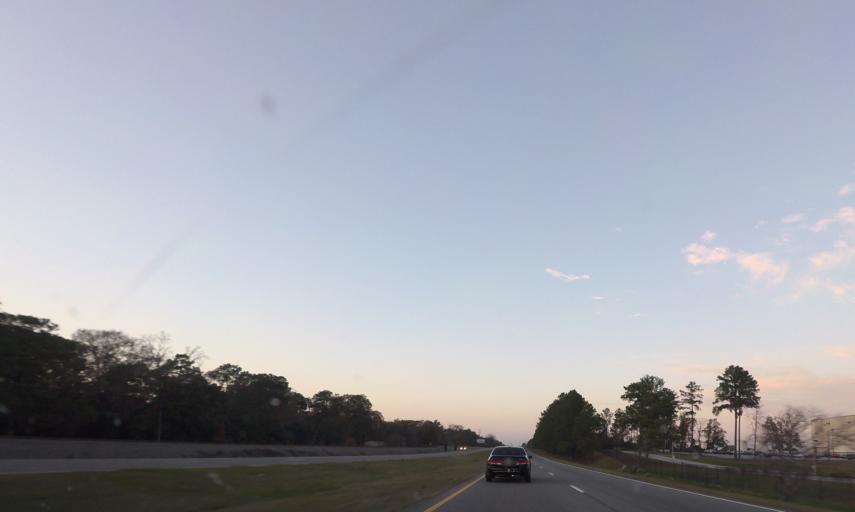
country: US
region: Georgia
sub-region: Houston County
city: Warner Robins
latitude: 32.6378
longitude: -83.6054
